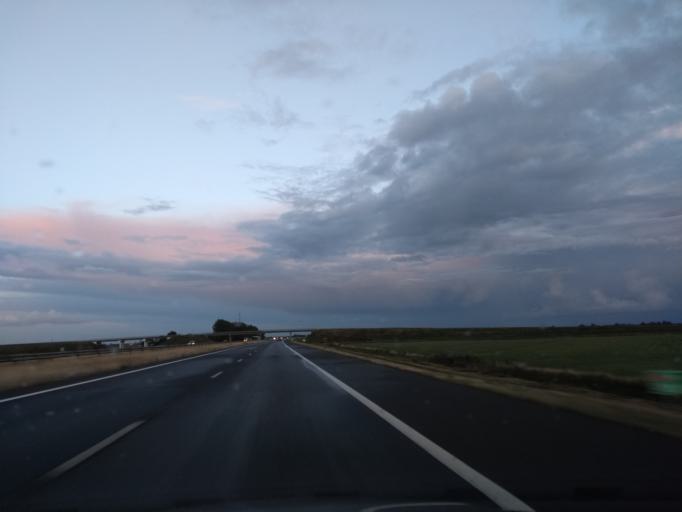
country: NL
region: Friesland
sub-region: Sudwest Fryslan
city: Oppenhuizen
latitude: 52.9881
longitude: 5.7234
